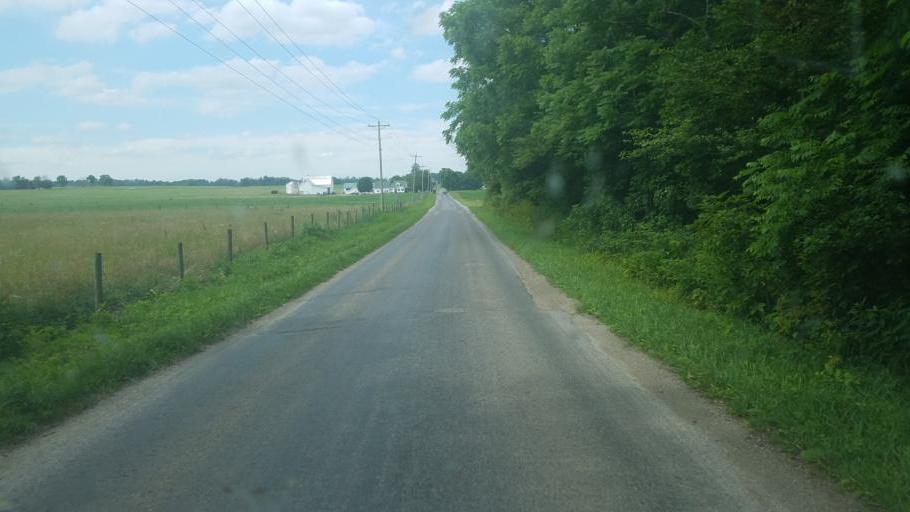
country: US
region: Ohio
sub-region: Knox County
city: Fredericktown
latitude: 40.5107
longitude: -82.6293
